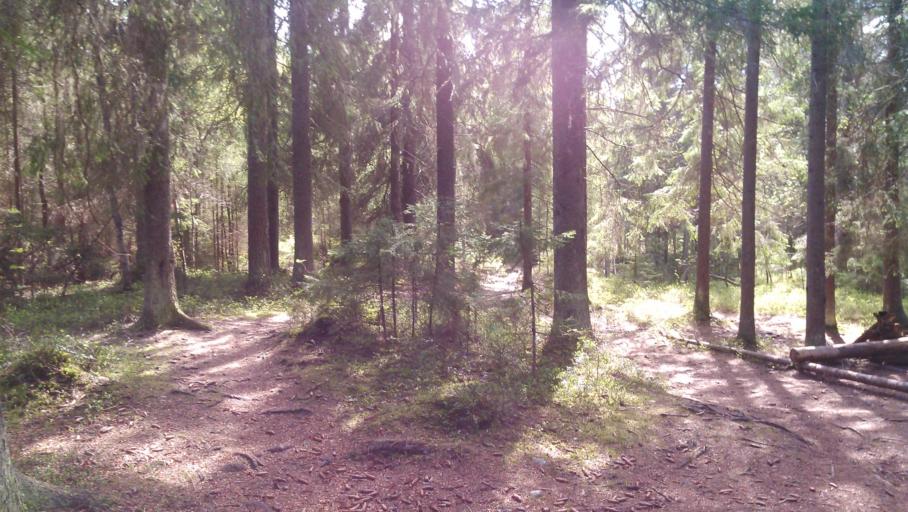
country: SE
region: Vaesterbotten
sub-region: Umea Kommun
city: Umea
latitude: 63.8387
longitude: 20.3029
